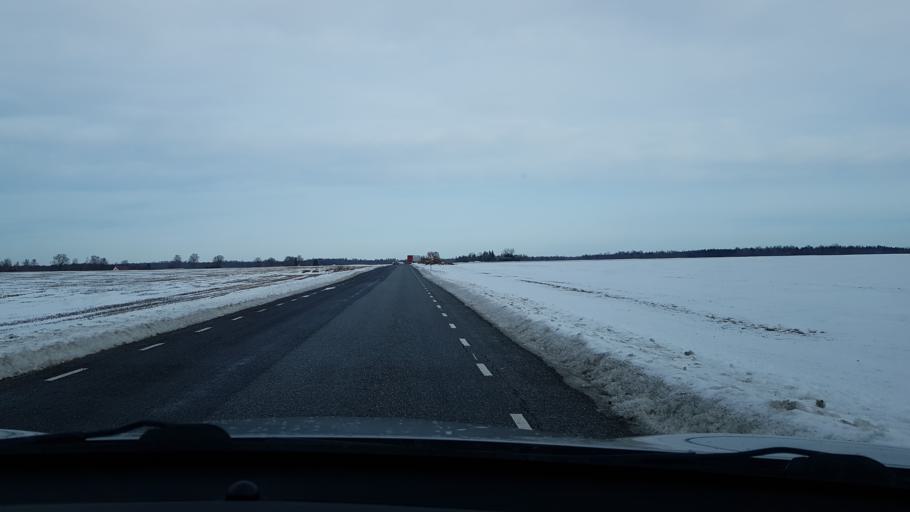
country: EE
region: Jaervamaa
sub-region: Paide linn
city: Paide
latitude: 58.8750
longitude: 25.6717
